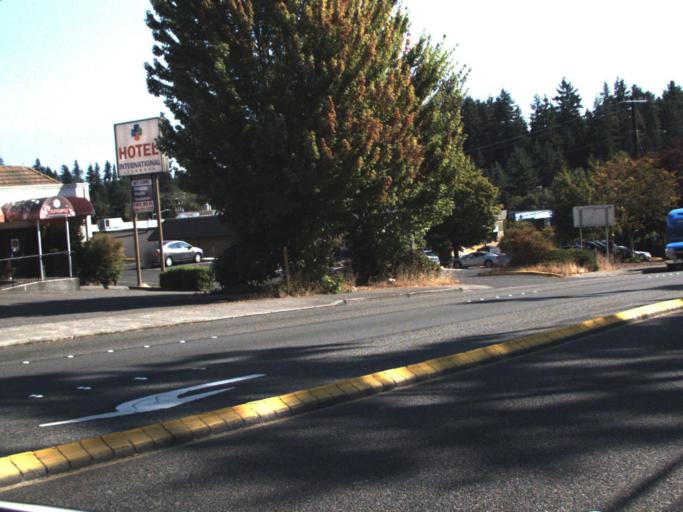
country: US
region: Washington
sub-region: Snohomish County
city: Lynnwood
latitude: 47.8212
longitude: -122.3097
